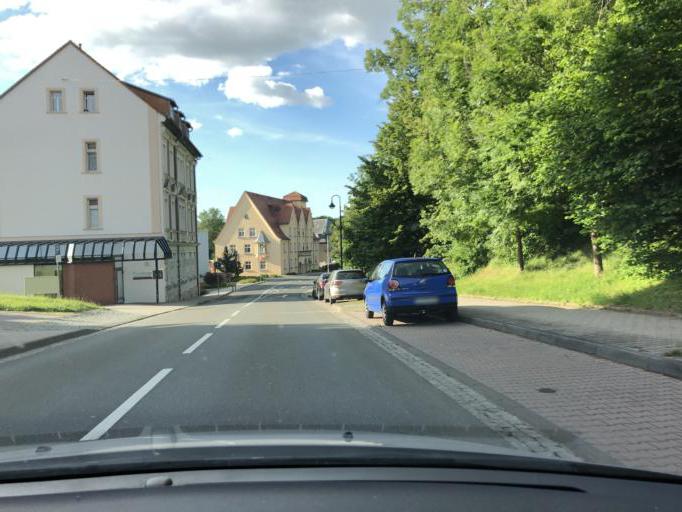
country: DE
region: Thuringia
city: Schmolln
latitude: 50.8986
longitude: 12.3587
